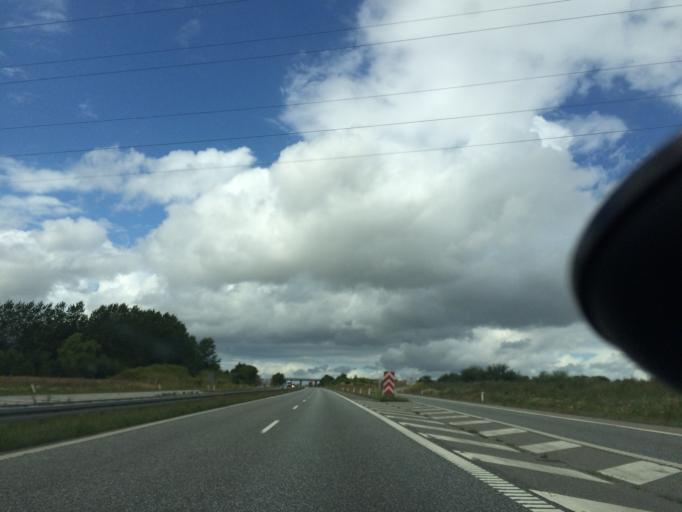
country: DK
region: Central Jutland
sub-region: Arhus Kommune
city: Framlev
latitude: 56.1534
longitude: 10.0152
